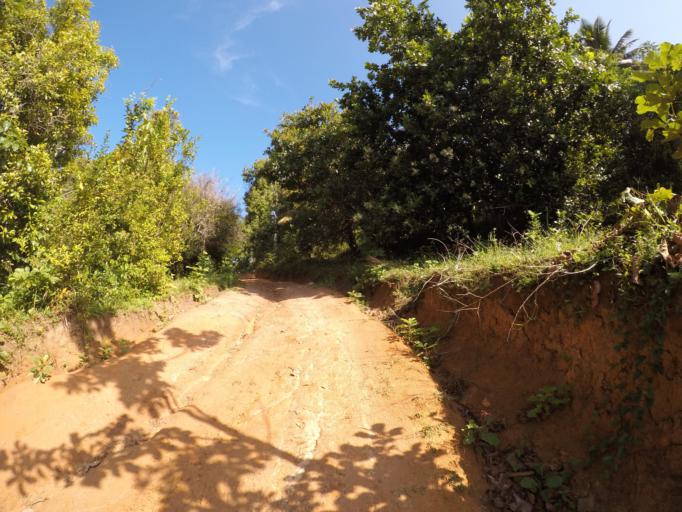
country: TZ
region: Pemba South
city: Mtambile
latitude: -5.3837
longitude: 39.7208
